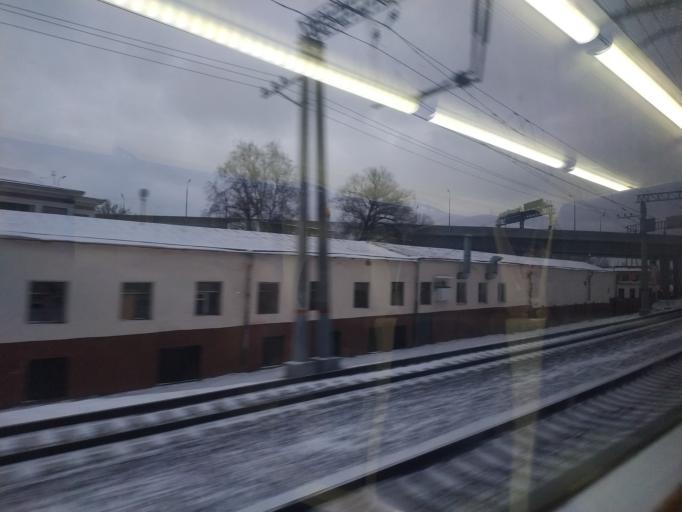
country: RU
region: Moscow
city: Lefortovo
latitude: 55.7387
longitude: 37.6951
